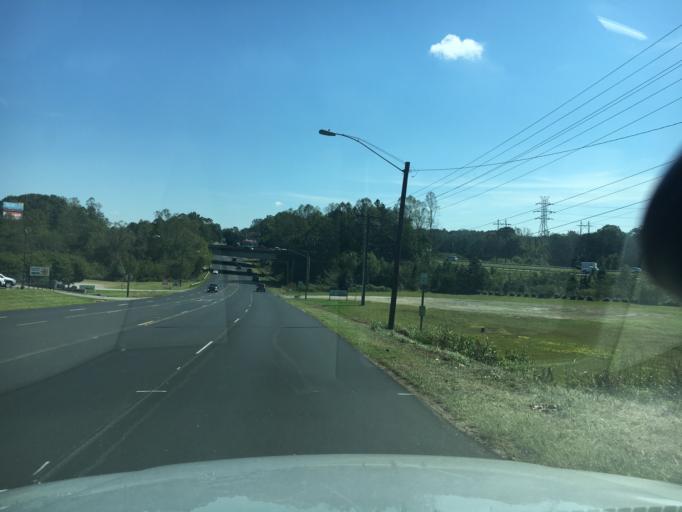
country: US
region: North Carolina
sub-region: Catawba County
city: Hickory
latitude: 35.7136
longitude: -81.3334
